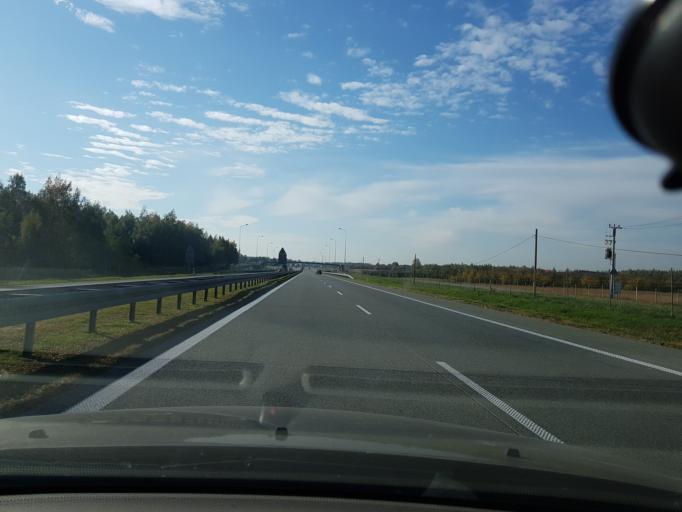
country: PL
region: Lodz Voivodeship
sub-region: Powiat skierniewicki
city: Kowiesy
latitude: 51.8712
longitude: 20.3860
